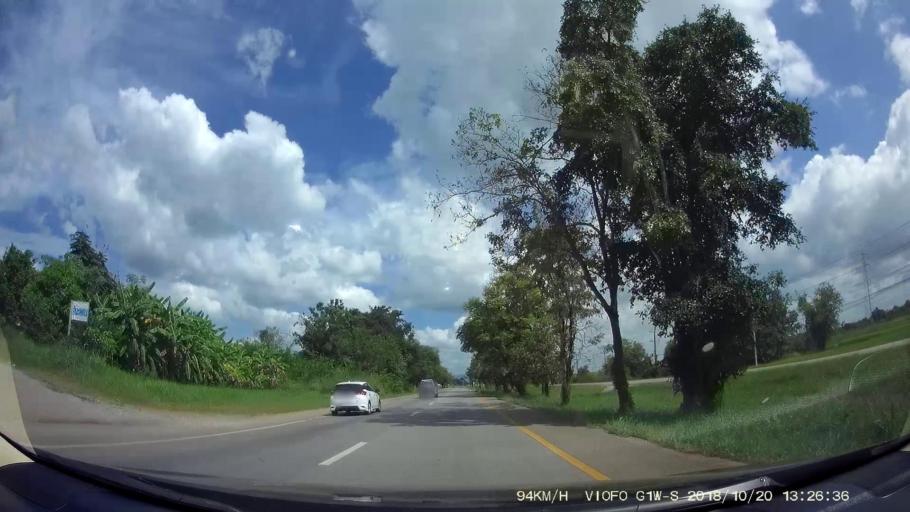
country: TH
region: Chaiyaphum
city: Khon San
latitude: 16.5936
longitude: 101.9486
